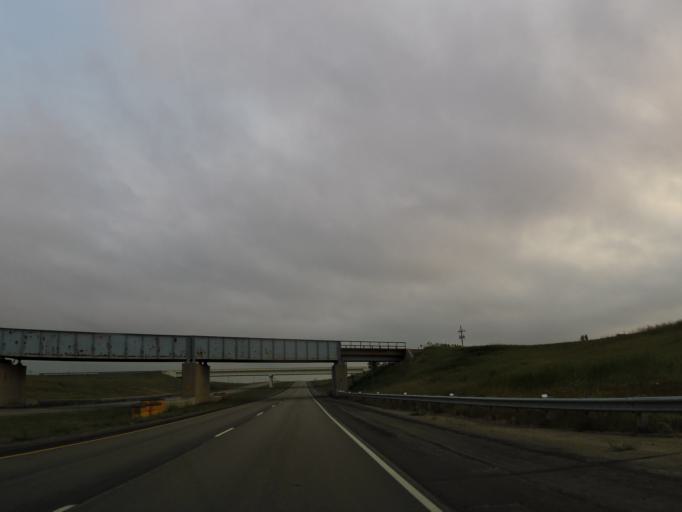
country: US
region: North Dakota
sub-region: Walsh County
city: Grafton
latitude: 48.5321
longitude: -97.1861
